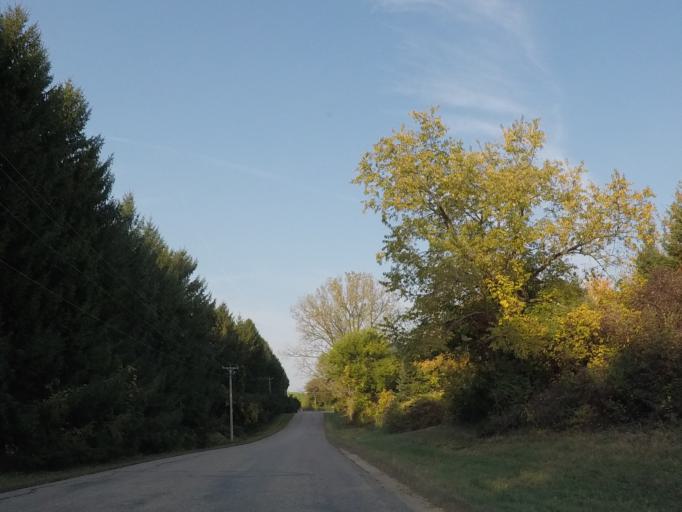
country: US
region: Wisconsin
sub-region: Dane County
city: Cross Plains
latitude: 43.0421
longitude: -89.6128
